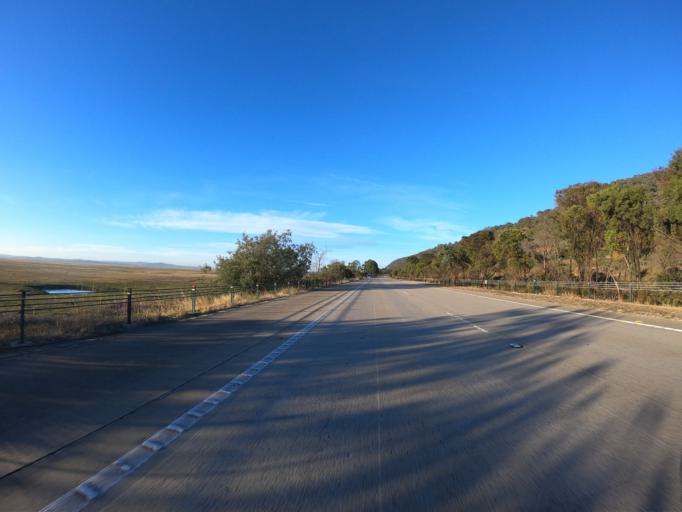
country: AU
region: New South Wales
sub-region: Yass Valley
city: Gundaroo
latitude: -35.0137
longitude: 149.3797
